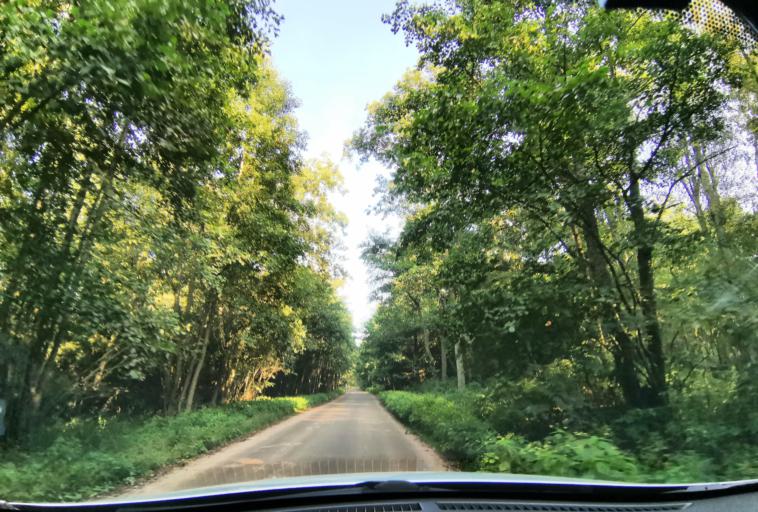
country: LT
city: Nida
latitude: 55.1631
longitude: 20.8206
